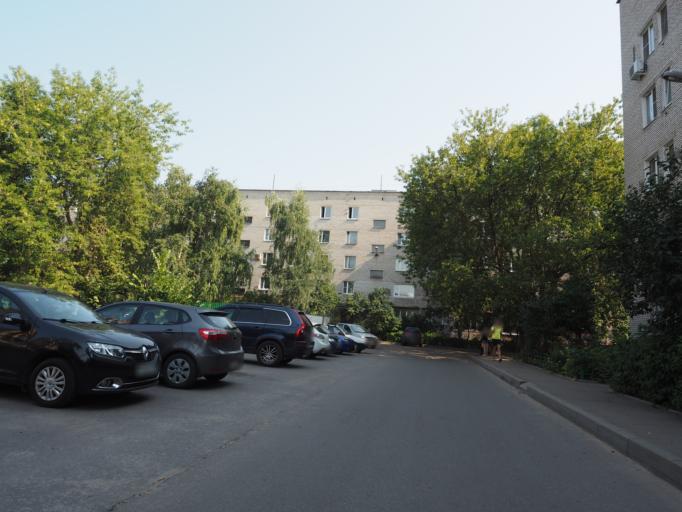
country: RU
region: Moskovskaya
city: Udel'naya
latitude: 55.6219
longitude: 38.0015
